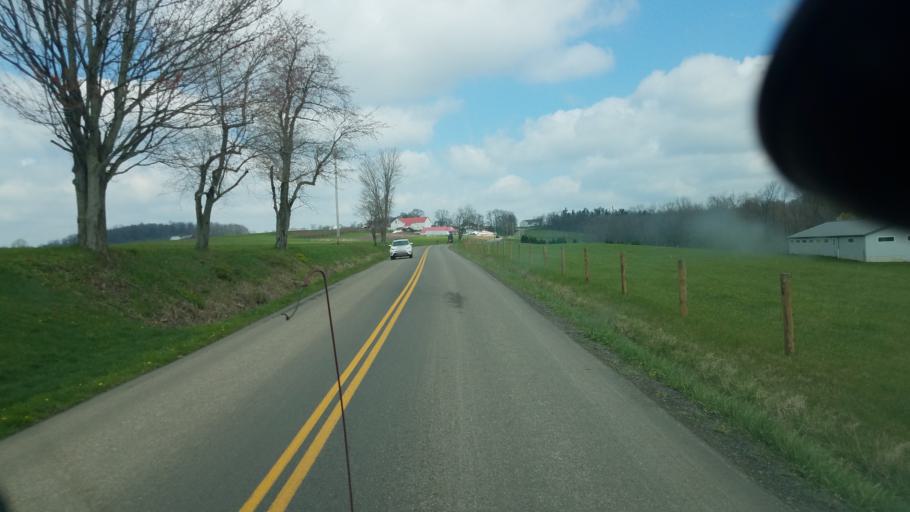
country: US
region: Ohio
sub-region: Holmes County
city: Millersburg
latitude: 40.6314
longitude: -81.8437
